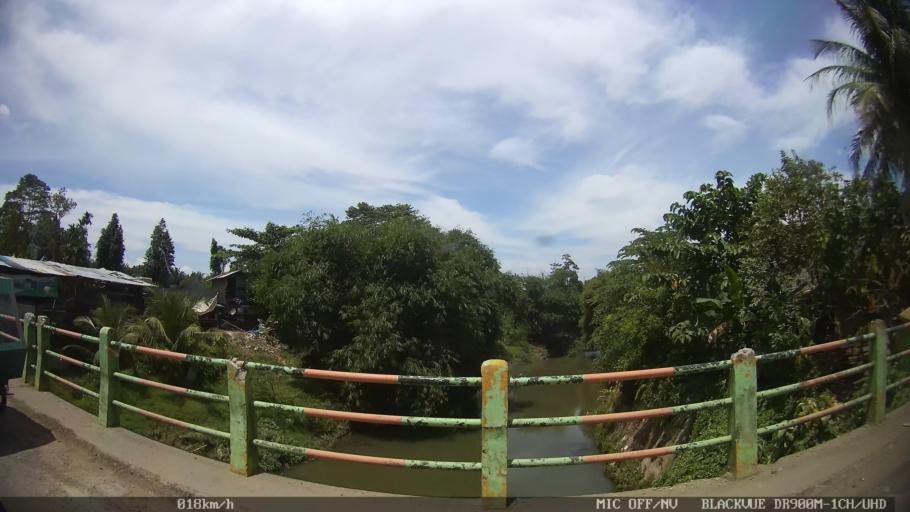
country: ID
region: North Sumatra
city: Binjai
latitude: 3.5921
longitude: 98.4971
